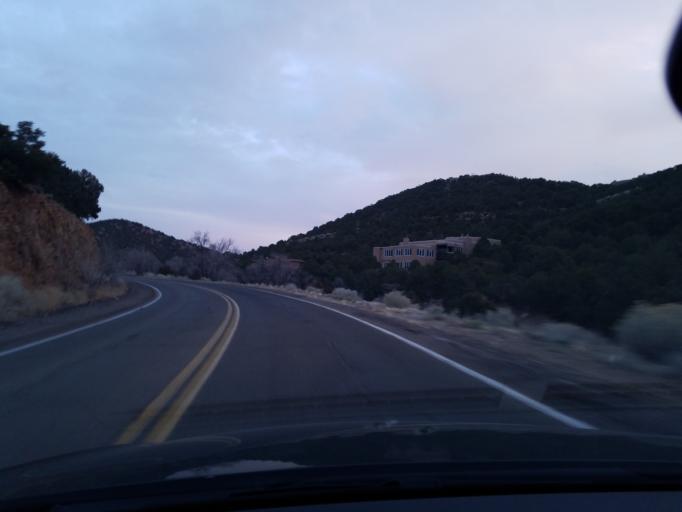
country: US
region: New Mexico
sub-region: Santa Fe County
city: Santa Fe
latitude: 35.6987
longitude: -105.9081
